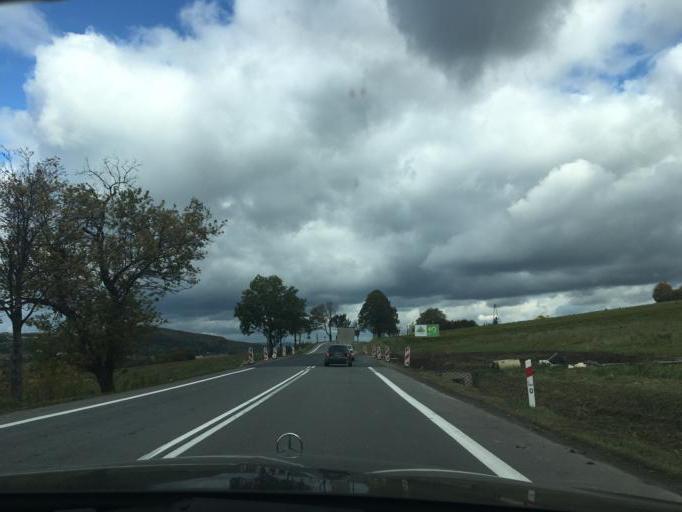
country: PL
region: Subcarpathian Voivodeship
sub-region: Powiat krosnienski
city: Dukla
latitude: 49.5849
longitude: 21.7052
